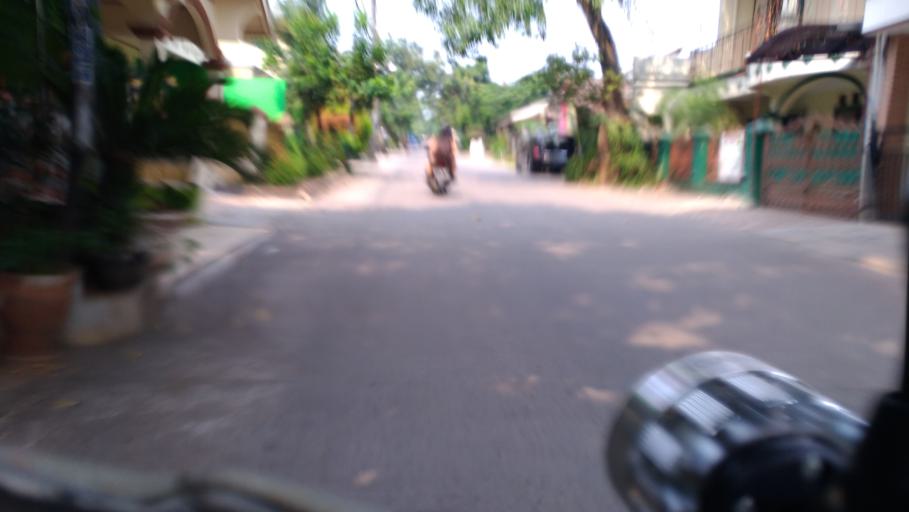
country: ID
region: West Java
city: Depok
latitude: -6.3628
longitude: 106.8751
